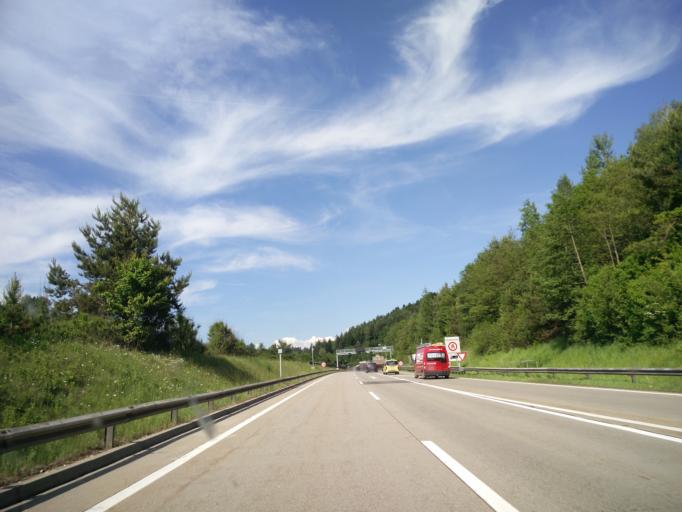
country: AT
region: Carinthia
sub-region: Klagenfurt am Woerthersee
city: Klagenfurt am Woerthersee
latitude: 46.6327
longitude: 14.2423
